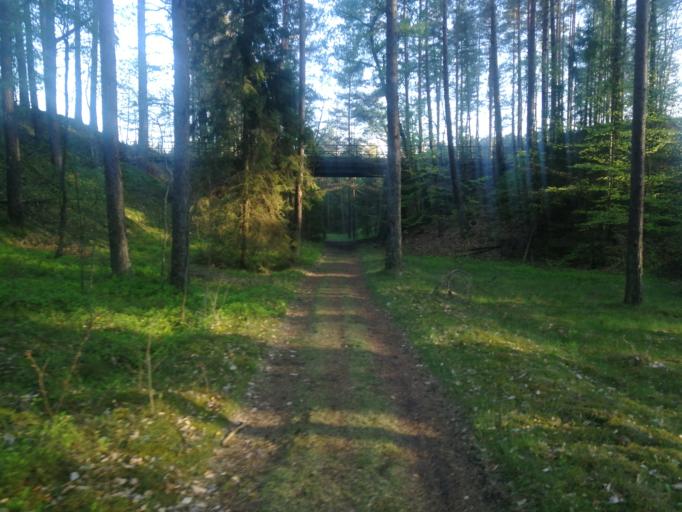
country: PL
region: Pomeranian Voivodeship
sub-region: Powiat bytowski
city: Czarna Dabrowka
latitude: 54.2612
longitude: 17.5779
